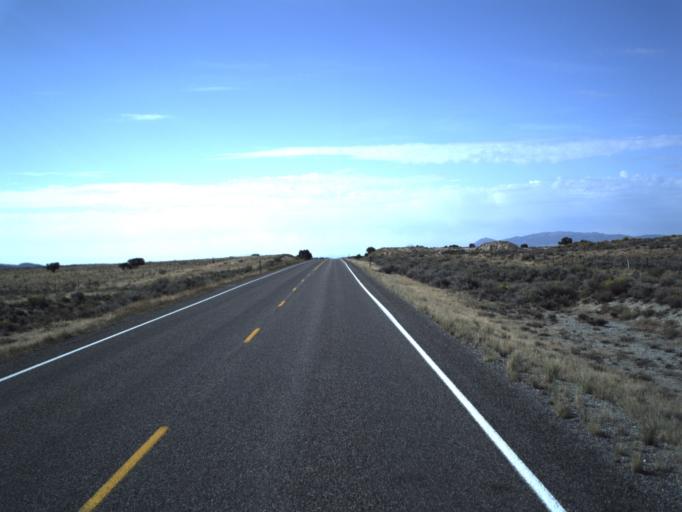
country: US
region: Idaho
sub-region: Cassia County
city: Burley
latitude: 41.7326
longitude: -113.5223
